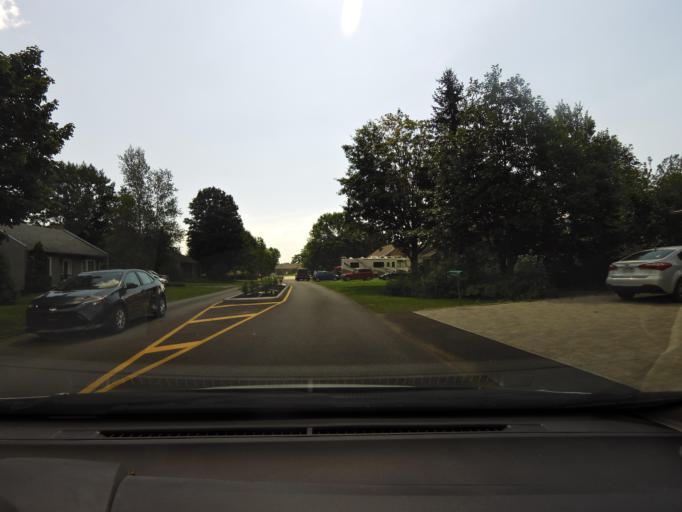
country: CA
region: Quebec
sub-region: Capitale-Nationale
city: Neuville
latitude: 46.7169
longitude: -71.5441
